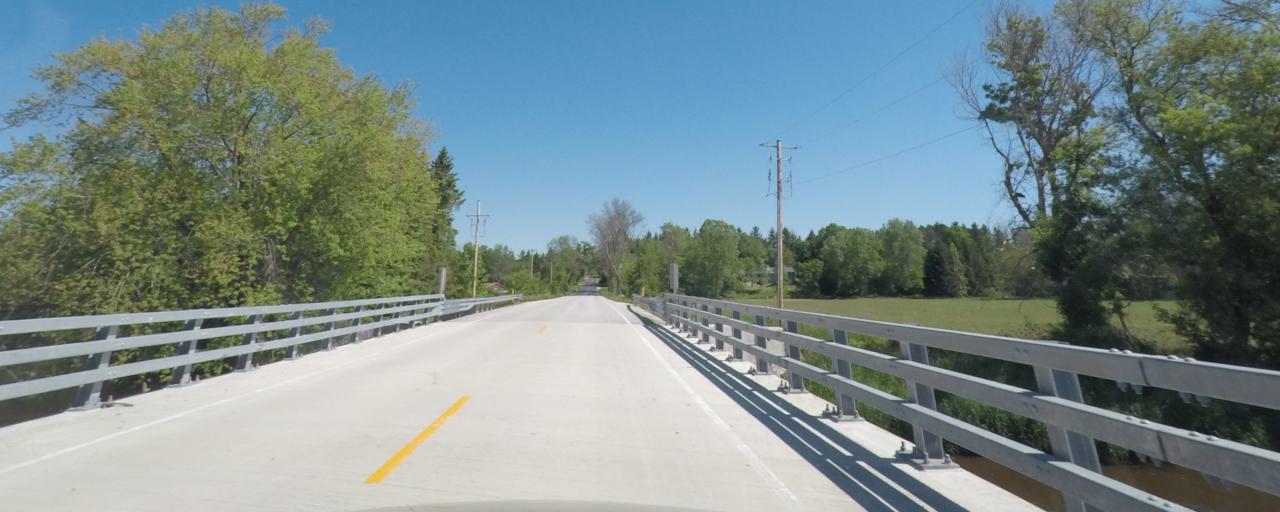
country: US
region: Wisconsin
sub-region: Sheboygan County
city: Sheboygan Falls
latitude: 43.7415
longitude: -87.8402
